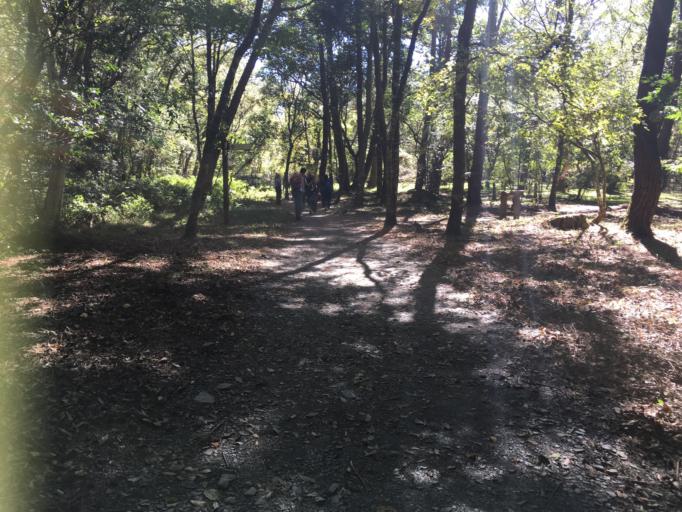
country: TW
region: Taiwan
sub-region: Nantou
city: Puli
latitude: 23.9482
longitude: 121.1875
